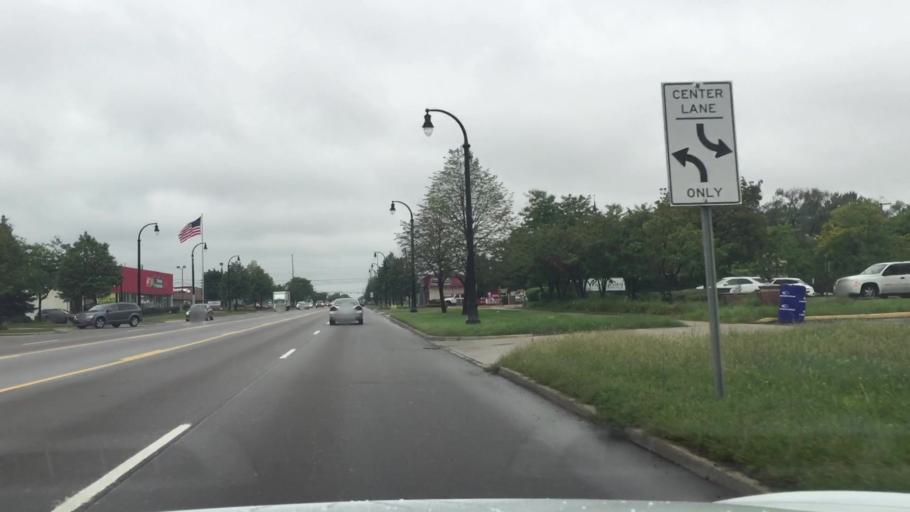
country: US
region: Michigan
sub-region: Wayne County
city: Livonia
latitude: 42.3694
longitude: -83.3277
